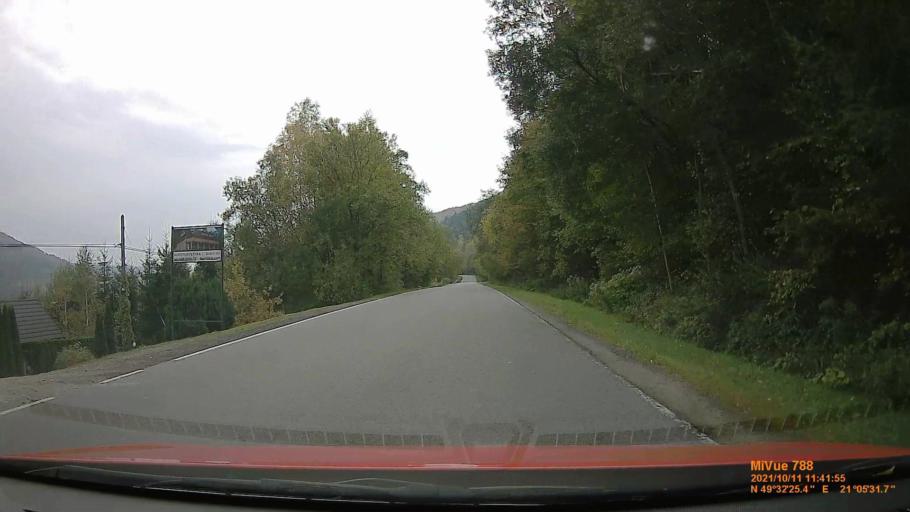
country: PL
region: Lesser Poland Voivodeship
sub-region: Powiat gorlicki
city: Uscie Gorlickie
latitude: 49.5403
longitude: 21.0923
